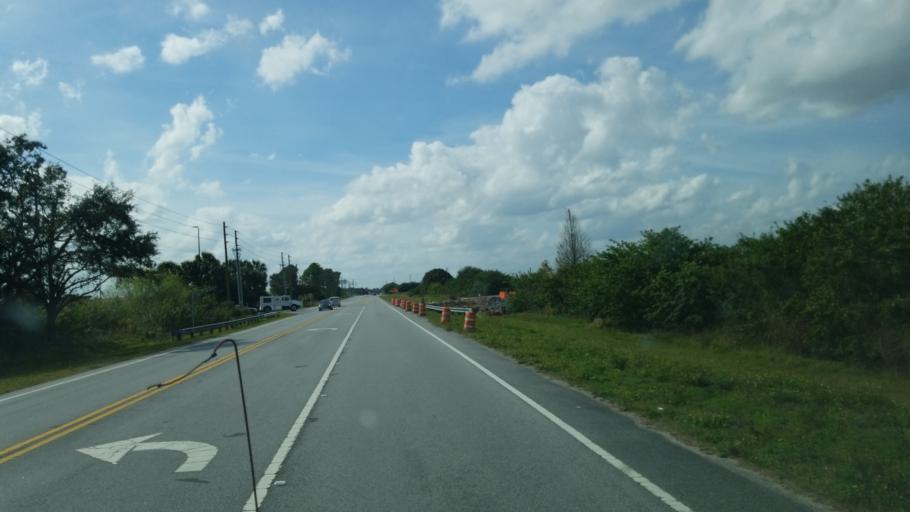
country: US
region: Florida
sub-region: Polk County
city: Lake Wales
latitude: 27.9572
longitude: -81.6144
